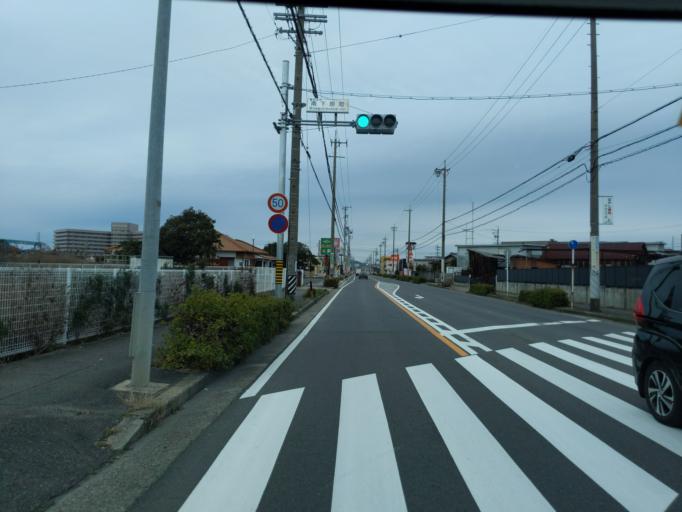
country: JP
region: Aichi
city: Kasugai
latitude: 35.2665
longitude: 136.9721
